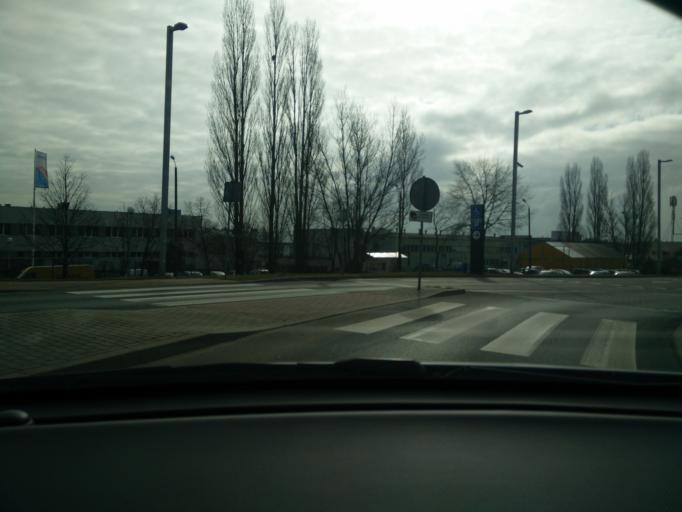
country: PL
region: Greater Poland Voivodeship
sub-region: Powiat poznanski
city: Lubon
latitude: 52.3540
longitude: 16.8896
